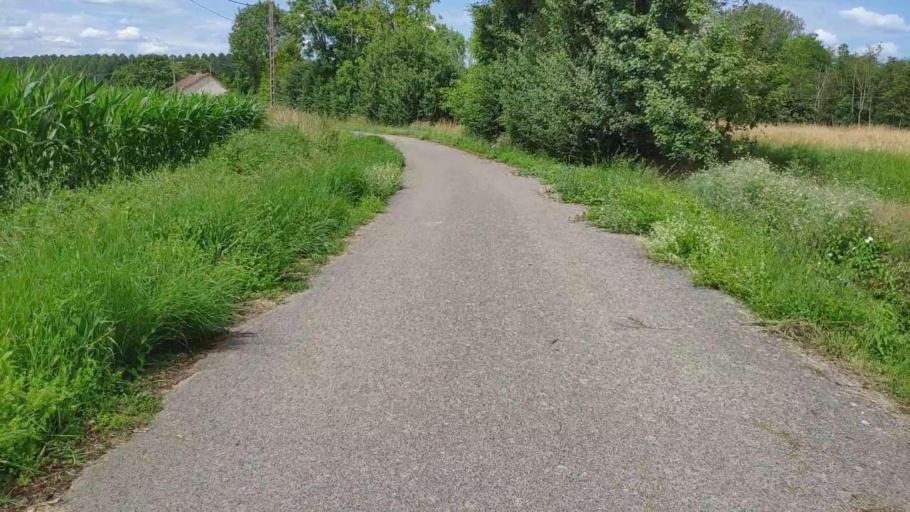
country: FR
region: Franche-Comte
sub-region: Departement du Jura
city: Chaussin
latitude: 46.8712
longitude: 5.4239
